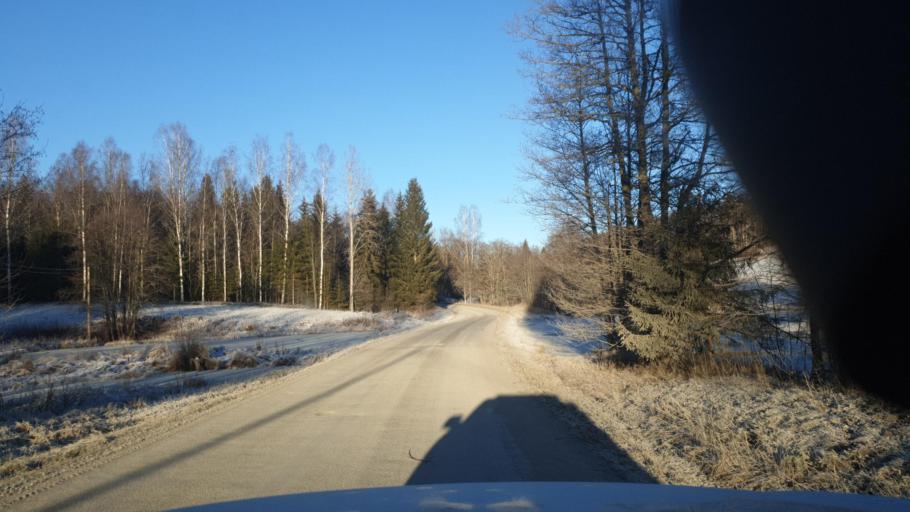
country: SE
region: Vaermland
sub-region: Sunne Kommun
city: Sunne
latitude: 59.6919
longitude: 12.8880
